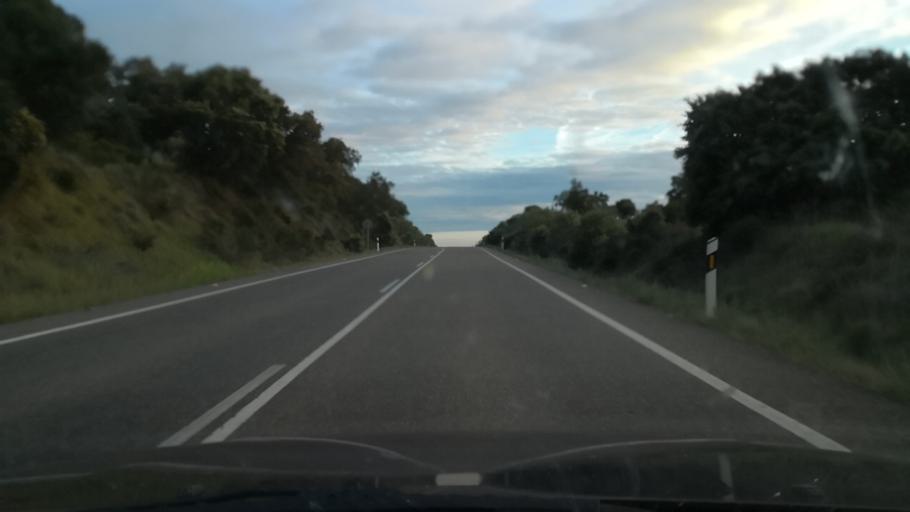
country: ES
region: Extremadura
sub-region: Provincia de Badajoz
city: La Roca de la Sierra
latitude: 39.1321
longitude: -6.6633
